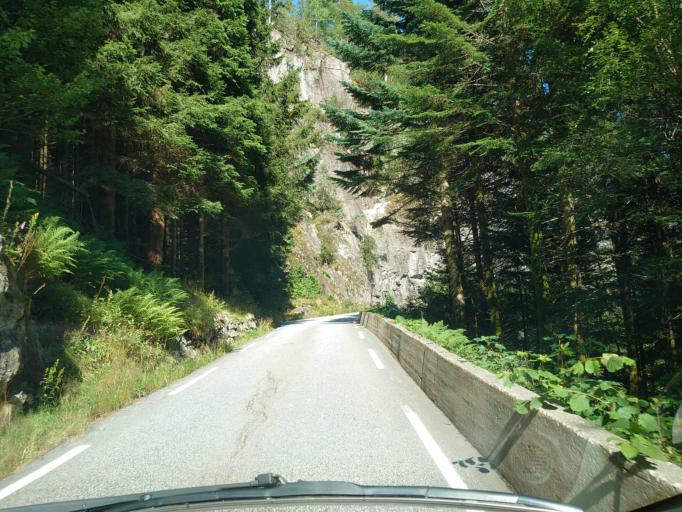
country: NO
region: Hordaland
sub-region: Vaksdal
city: Dale
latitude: 60.5867
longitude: 5.8395
